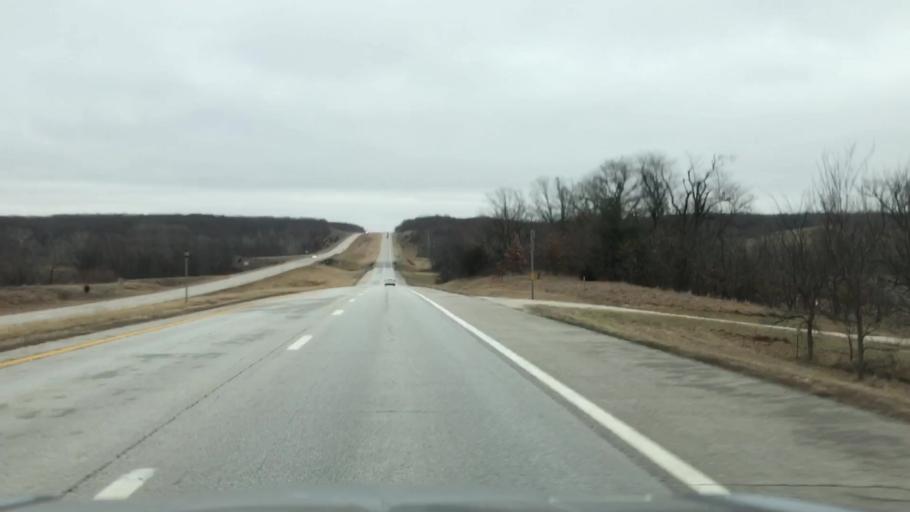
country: US
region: Missouri
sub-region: Linn County
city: Marceline
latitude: 39.7590
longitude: -92.8609
